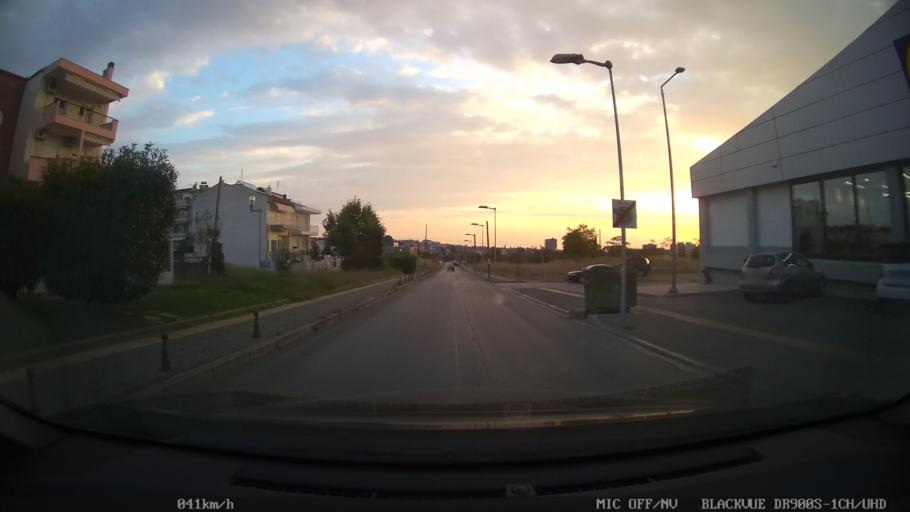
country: GR
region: Central Macedonia
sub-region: Nomos Thessalonikis
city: Pylaia
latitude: 40.6076
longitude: 22.9895
